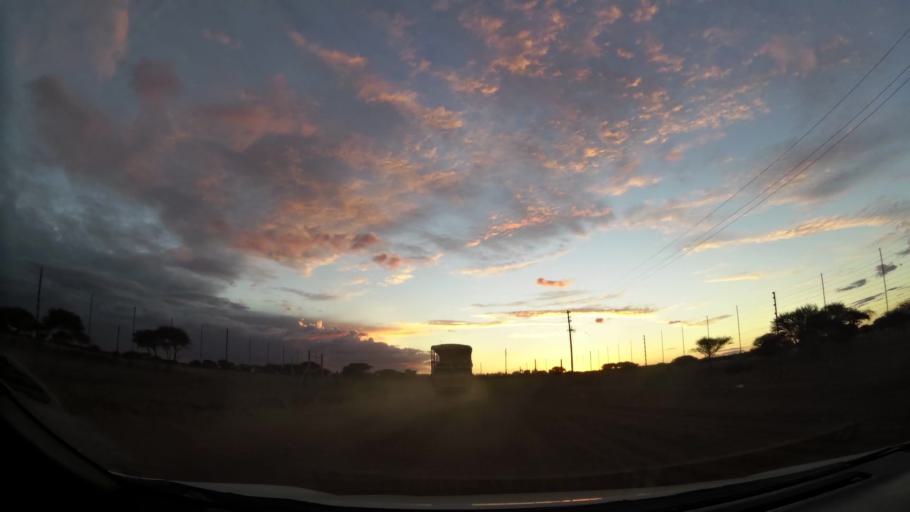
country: ZA
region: Limpopo
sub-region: Capricorn District Municipality
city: Polokwane
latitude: -23.7360
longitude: 29.4320
